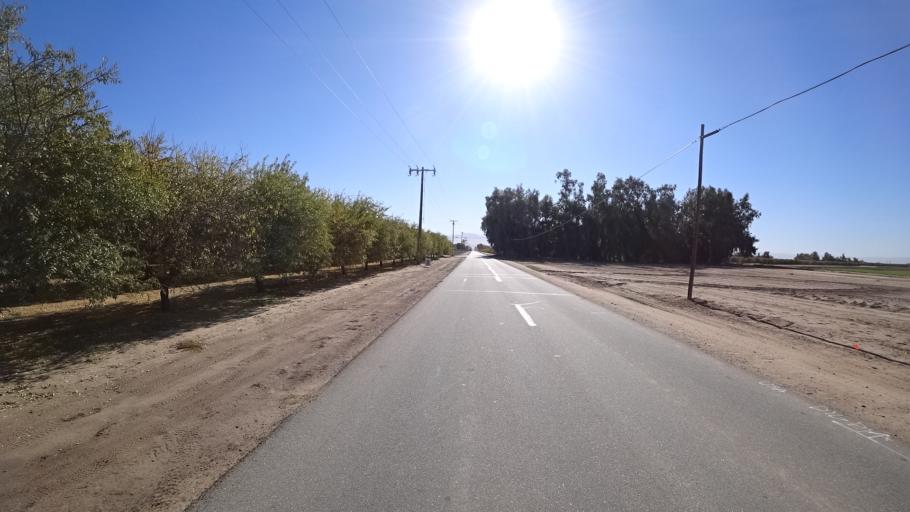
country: US
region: California
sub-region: Kern County
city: Greenfield
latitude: 35.2536
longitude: -119.0744
